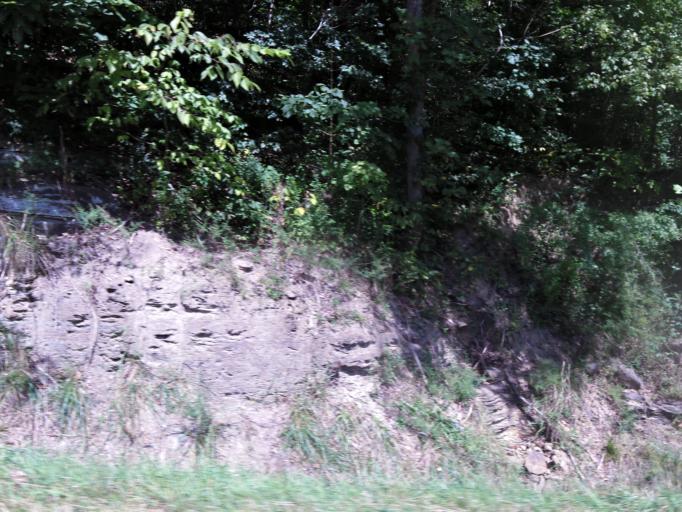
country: US
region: Kentucky
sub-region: Leslie County
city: Hyden
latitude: 37.1487
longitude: -83.3773
